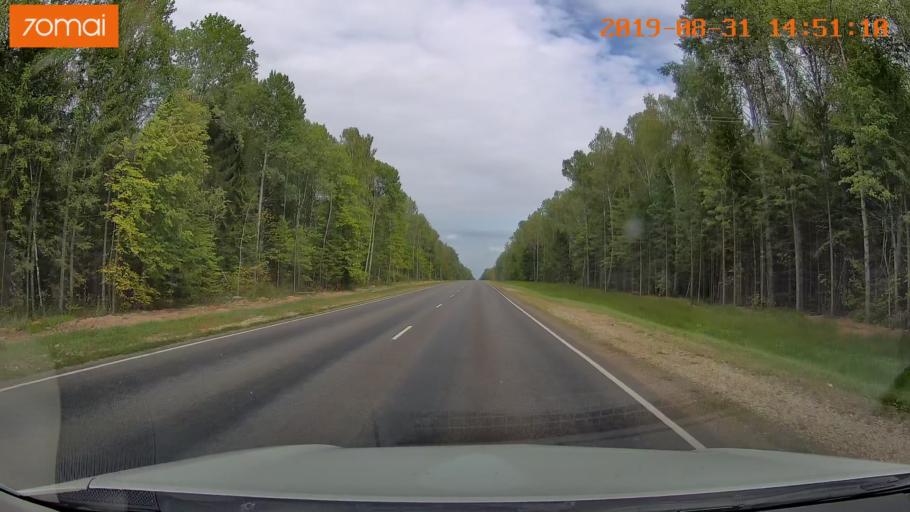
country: RU
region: Kaluga
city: Spas-Demensk
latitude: 54.2667
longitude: 33.8079
